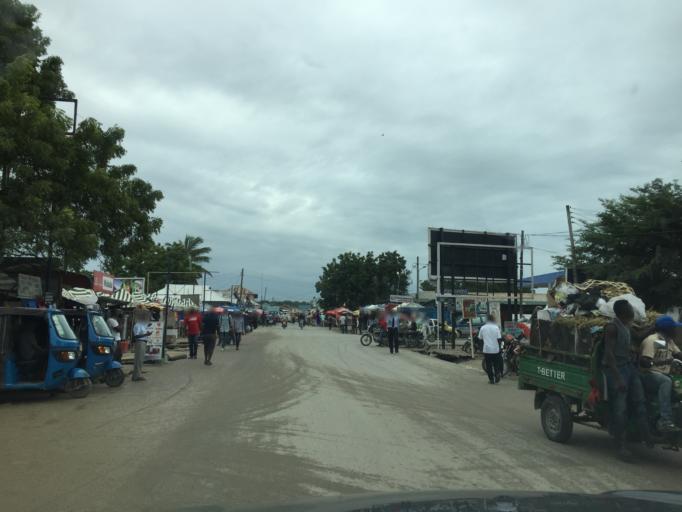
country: TZ
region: Dar es Salaam
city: Dar es Salaam
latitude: -6.8241
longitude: 39.3035
